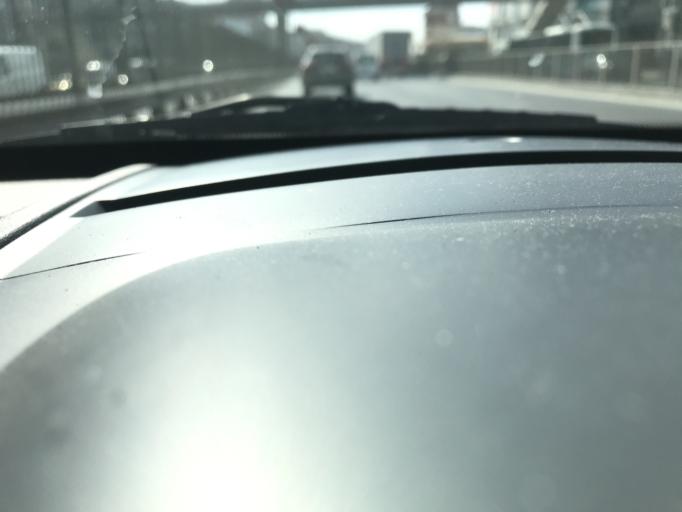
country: TR
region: Istanbul
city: Samandira
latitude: 41.0139
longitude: 29.1972
